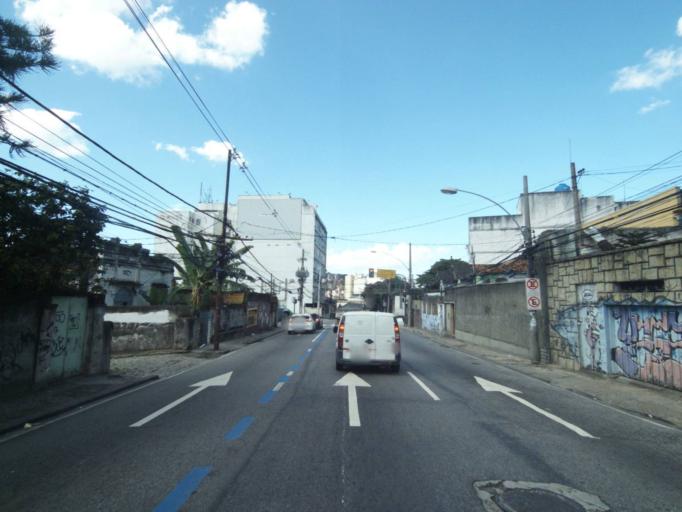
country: BR
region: Rio de Janeiro
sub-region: Rio De Janeiro
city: Rio de Janeiro
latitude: -22.9032
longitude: -43.2467
